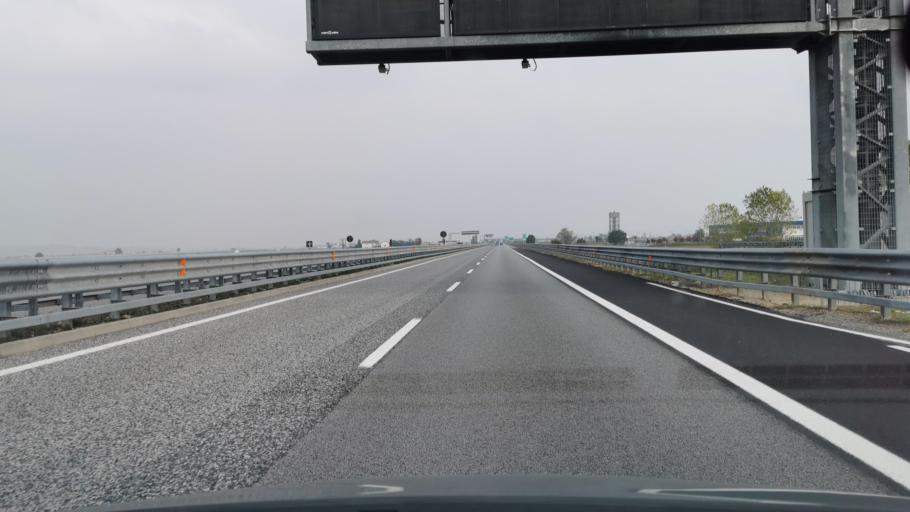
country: IT
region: Piedmont
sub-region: Provincia di Cuneo
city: Cervere
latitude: 44.6633
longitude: 7.7879
